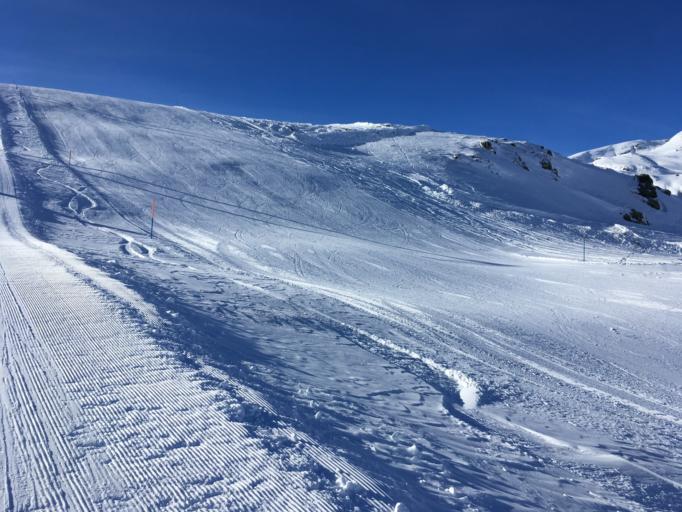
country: CH
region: Grisons
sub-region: Maloja District
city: Promontogno
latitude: 46.4543
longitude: 9.6450
